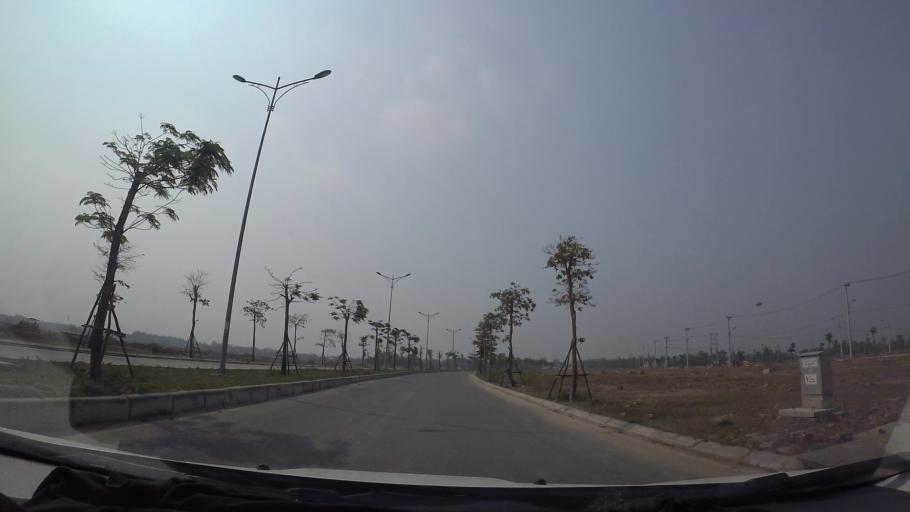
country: VN
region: Da Nang
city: Ngu Hanh Son
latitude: 15.9987
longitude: 108.2477
